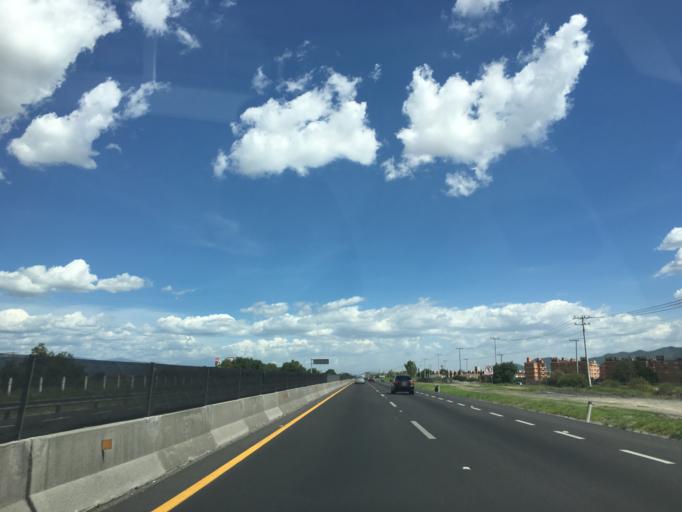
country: MX
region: Mexico
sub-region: Tonanitla
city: Colonia la Asuncion
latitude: 19.6872
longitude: -99.0769
